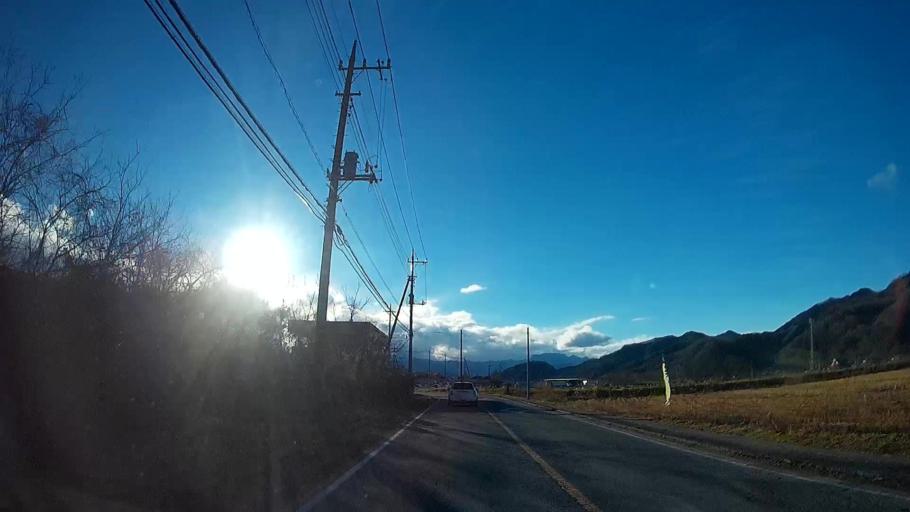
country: JP
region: Saitama
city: Chichibu
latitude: 36.0572
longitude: 139.0713
